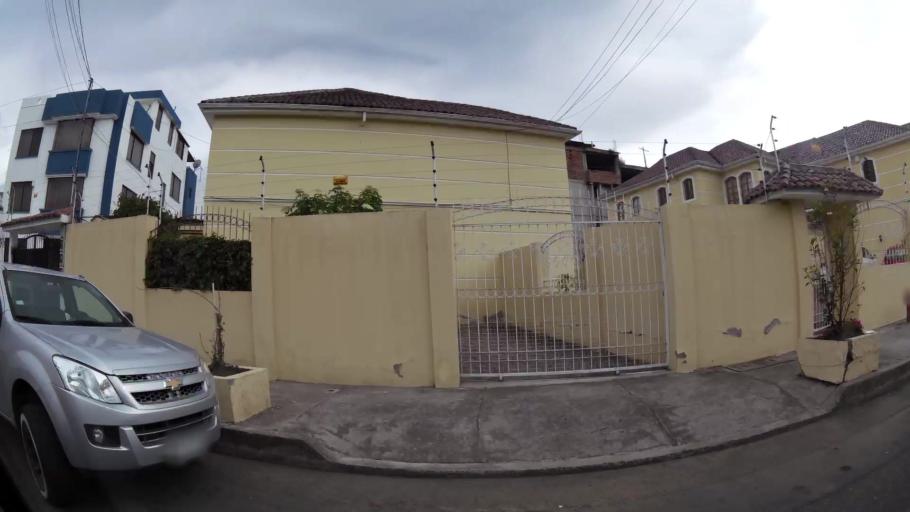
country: EC
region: Tungurahua
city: Ambato
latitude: -1.2588
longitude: -78.6364
